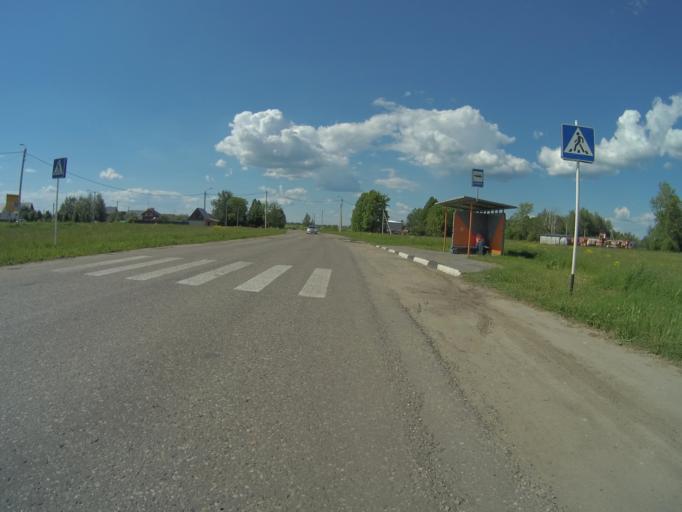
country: RU
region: Vladimir
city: Suzdal'
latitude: 56.4372
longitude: 40.4398
